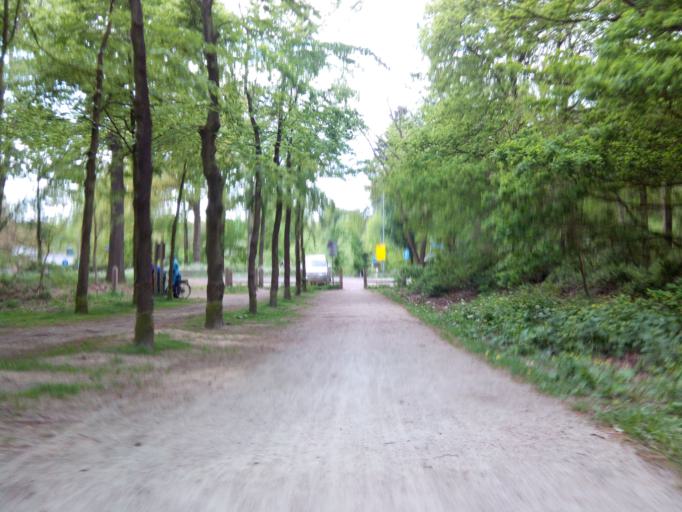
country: NL
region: Gelderland
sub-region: Gemeente Ede
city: Ede
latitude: 52.0552
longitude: 5.6547
